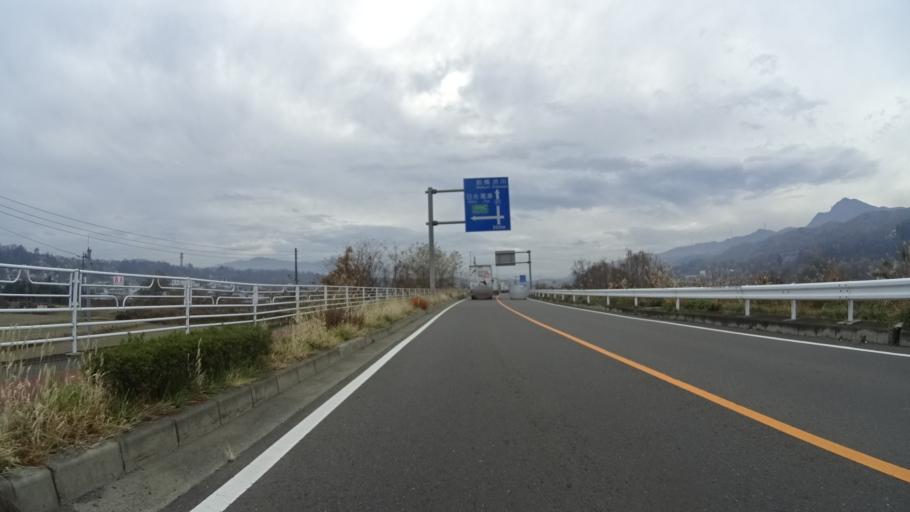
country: JP
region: Gunma
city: Numata
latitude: 36.6475
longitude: 139.0272
